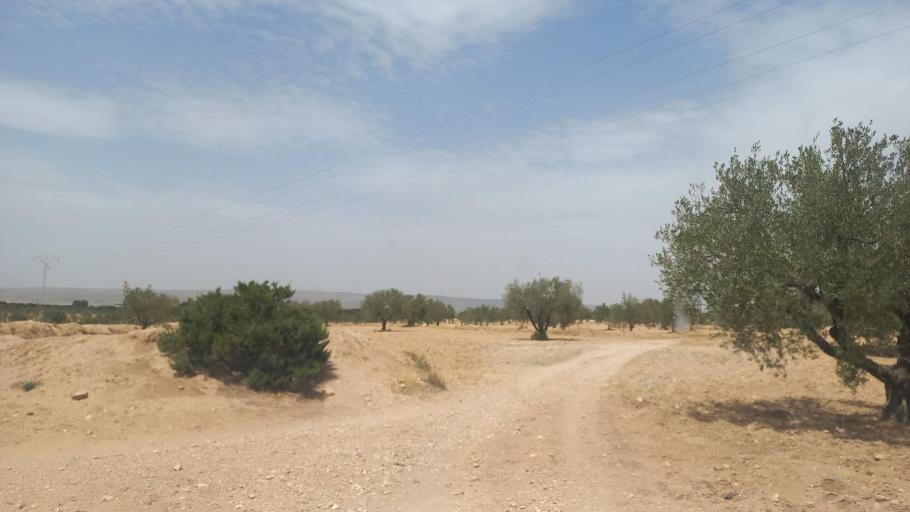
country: TN
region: Al Qasrayn
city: Kasserine
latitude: 35.2655
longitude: 8.9844
